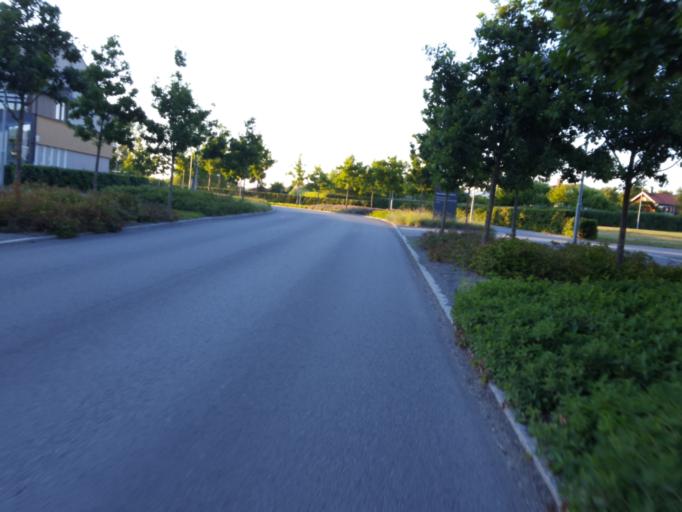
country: SE
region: Uppsala
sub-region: Uppsala Kommun
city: Saevja
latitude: 59.8177
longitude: 17.6593
